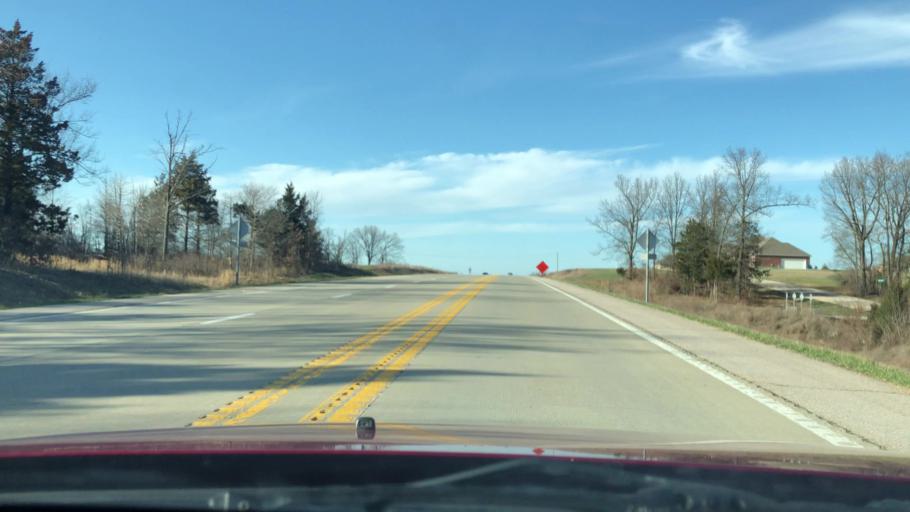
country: US
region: Missouri
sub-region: Camden County
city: Camdenton
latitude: 37.9468
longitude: -92.7156
